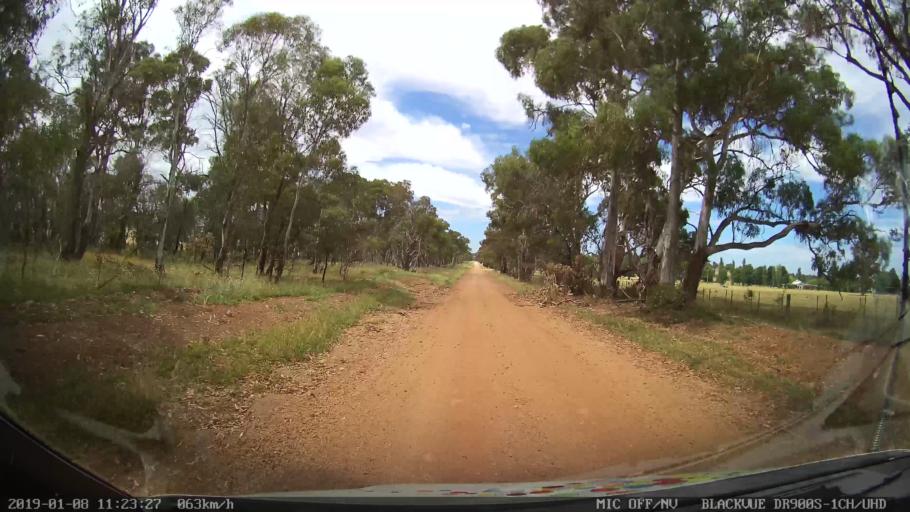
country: AU
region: New South Wales
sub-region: Guyra
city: Guyra
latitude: -30.2554
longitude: 151.5589
